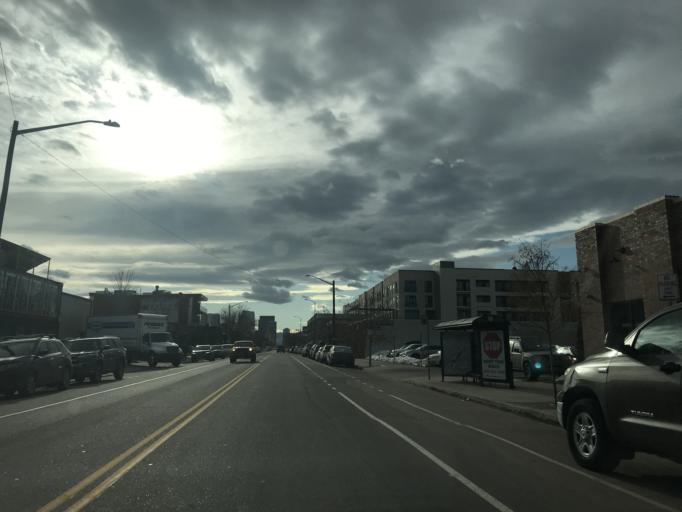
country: US
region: Colorado
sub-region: Denver County
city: Denver
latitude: 39.7659
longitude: -104.9759
